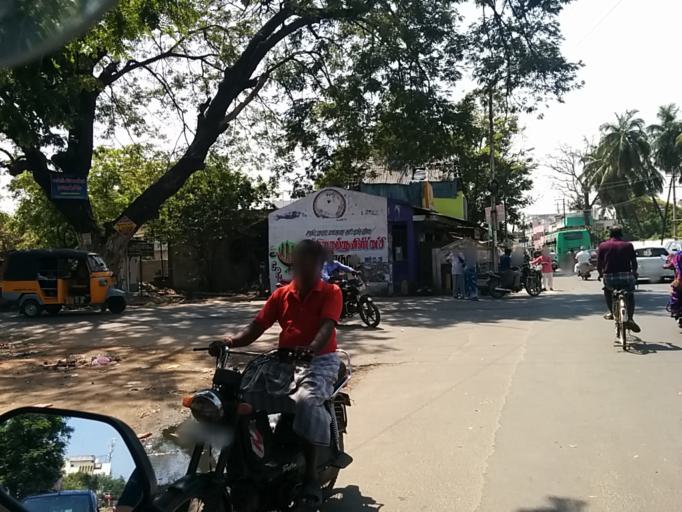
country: IN
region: Pondicherry
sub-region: Puducherry
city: Puducherry
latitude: 11.9317
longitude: 79.8055
